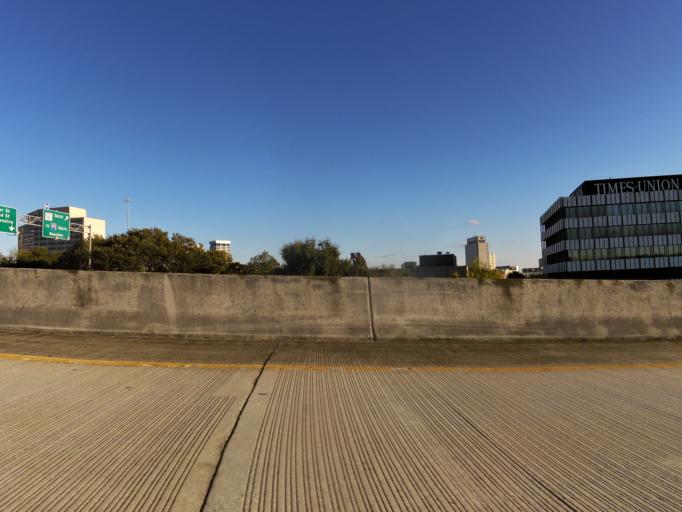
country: US
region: Florida
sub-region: Duval County
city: Jacksonville
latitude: 30.3254
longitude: -81.6683
